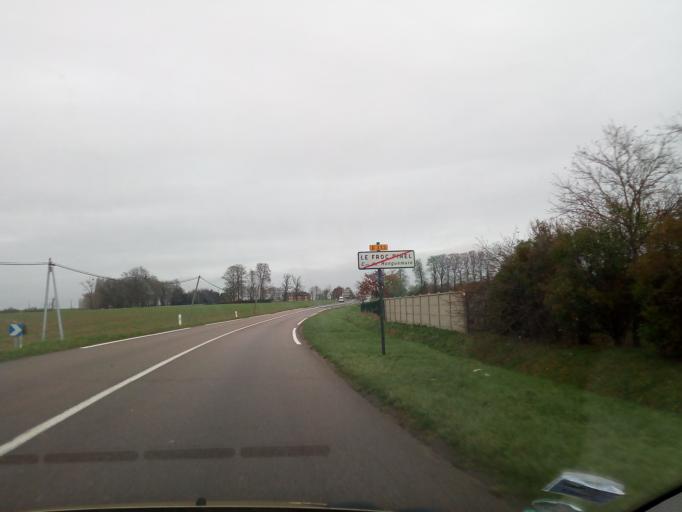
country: FR
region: Haute-Normandie
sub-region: Departement de l'Eure
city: Hauville
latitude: 49.3853
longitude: 0.7991
